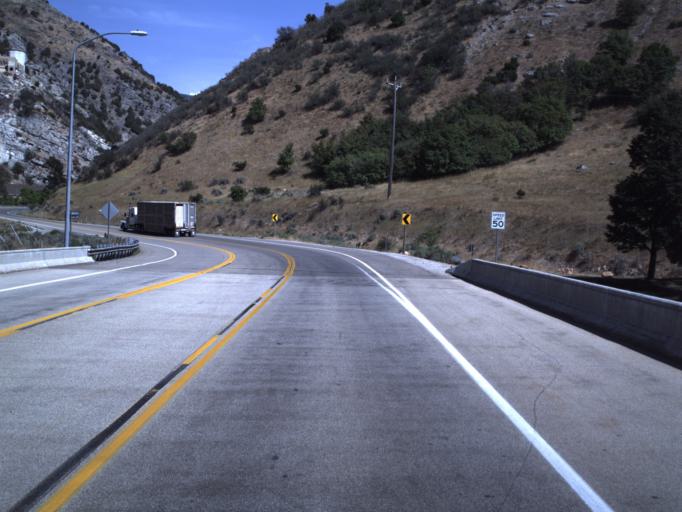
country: US
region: Utah
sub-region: Cache County
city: North Logan
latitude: 41.7429
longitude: -111.7868
